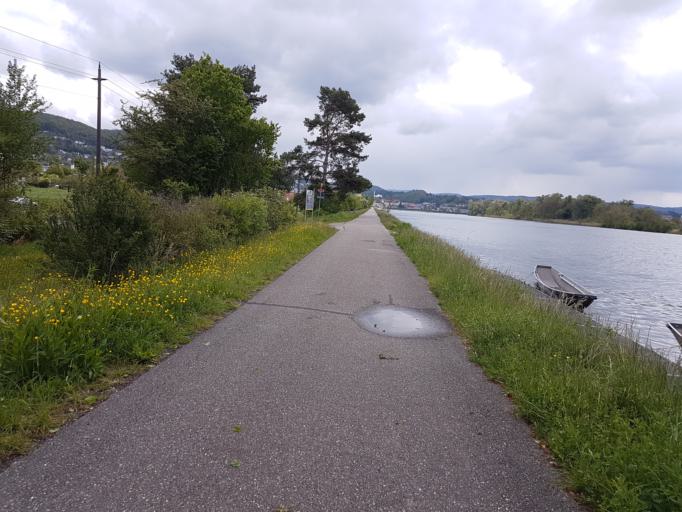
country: CH
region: Aargau
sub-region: Bezirk Zurzach
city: Klingnau
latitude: 47.5806
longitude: 8.2442
